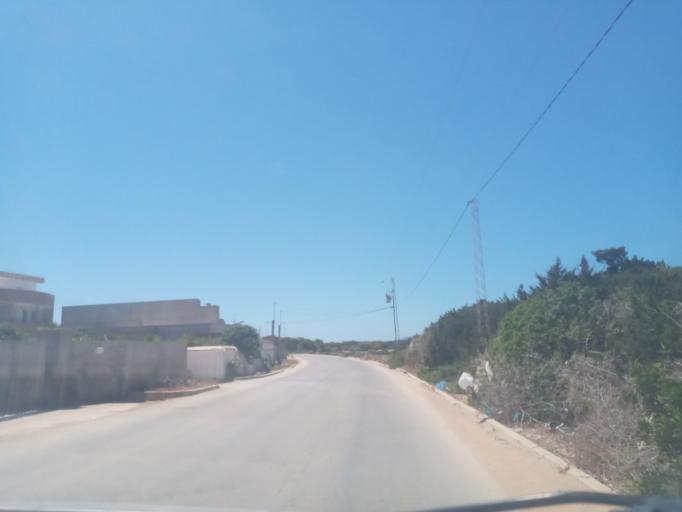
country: TN
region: Nabul
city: El Haouaria
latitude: 37.0493
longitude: 10.9700
